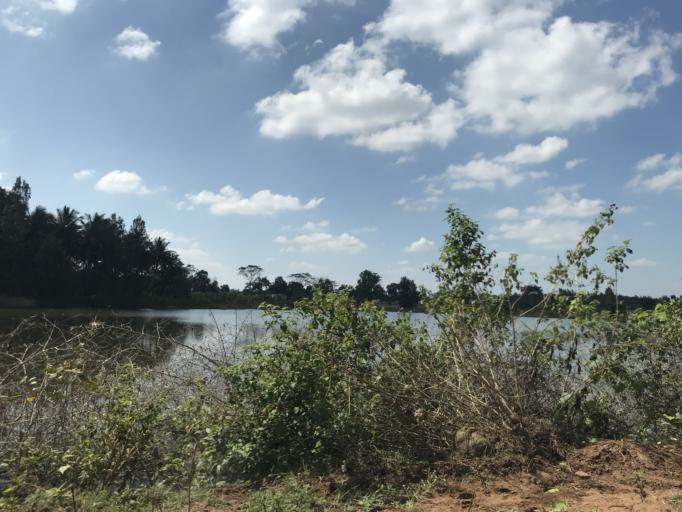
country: IN
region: Karnataka
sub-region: Mysore
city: Heggadadevankote
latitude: 12.1525
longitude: 76.2859
